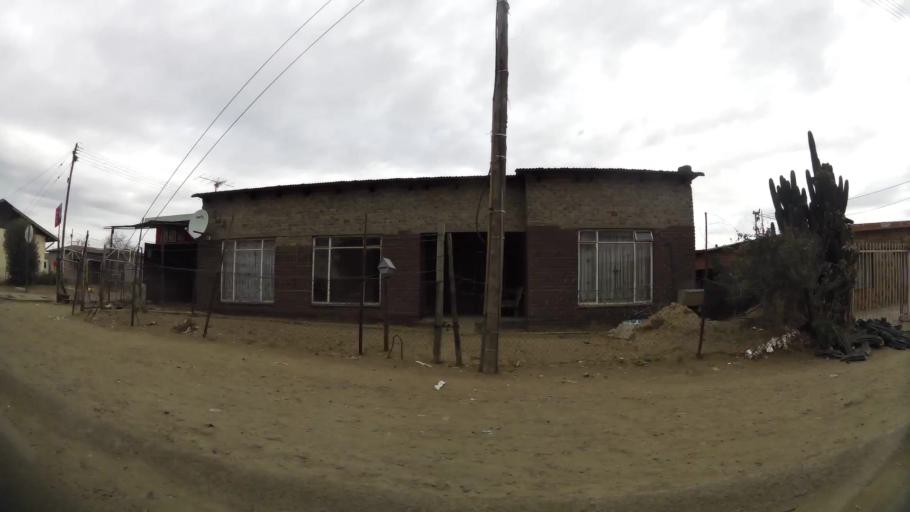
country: ZA
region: Orange Free State
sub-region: Fezile Dabi District Municipality
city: Kroonstad
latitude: -27.6468
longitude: 27.1952
